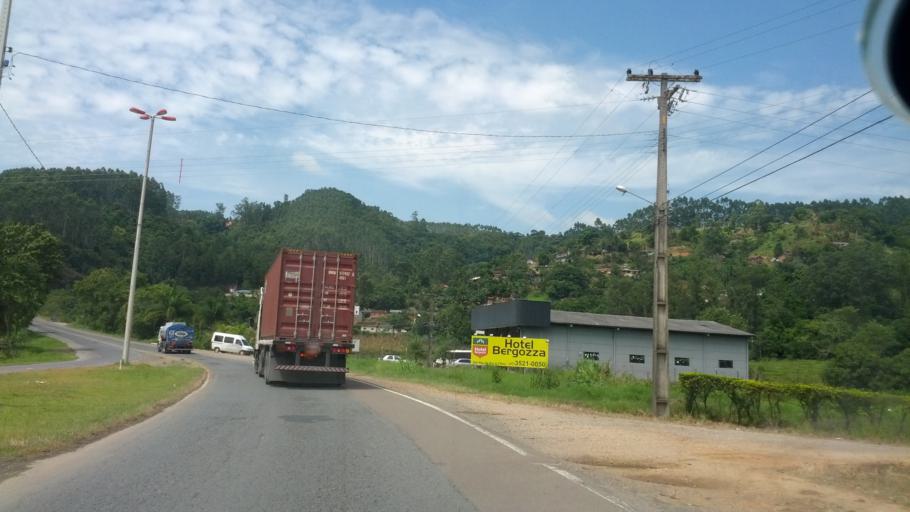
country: BR
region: Santa Catarina
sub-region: Ibirama
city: Ibirama
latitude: -27.0831
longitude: -49.5209
